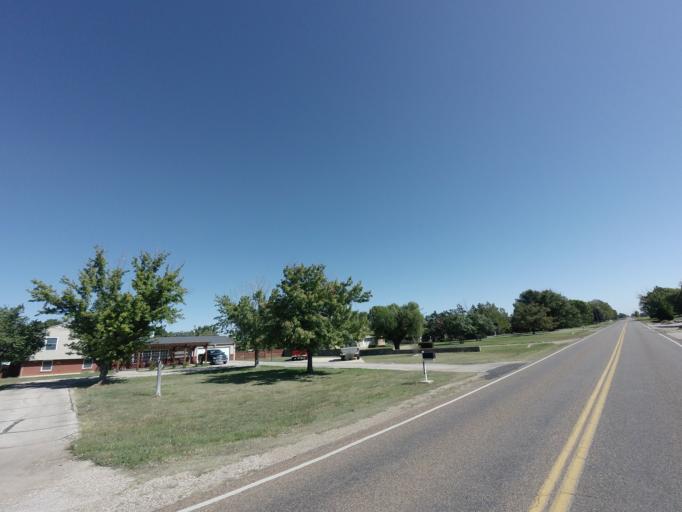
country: US
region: New Mexico
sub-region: Curry County
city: Clovis
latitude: 34.4193
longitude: -103.1763
